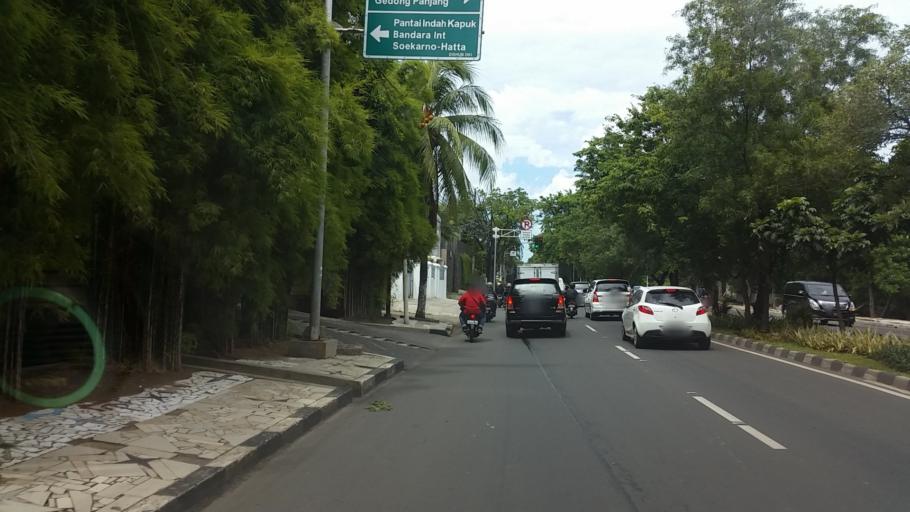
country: ID
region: Jakarta Raya
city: Jakarta
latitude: -6.1231
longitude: 106.7942
